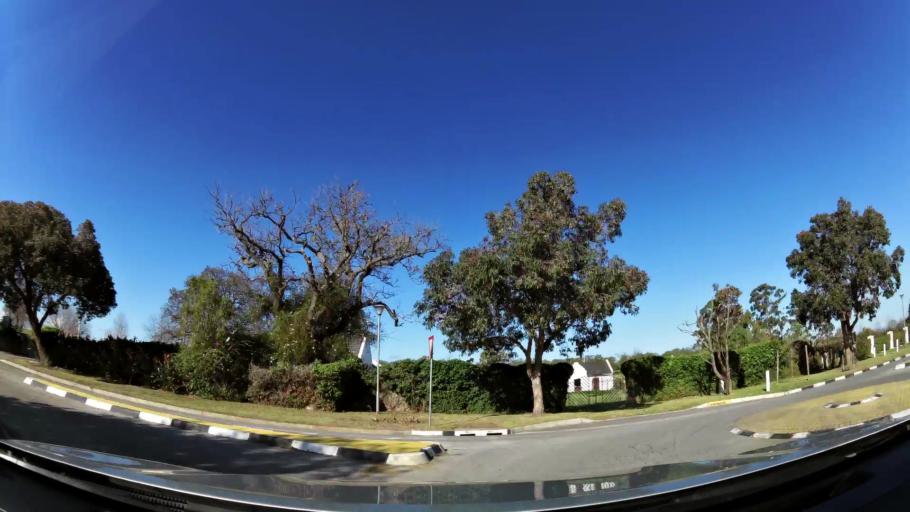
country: ZA
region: Western Cape
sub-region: Eden District Municipality
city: George
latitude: -33.9498
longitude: 22.4146
